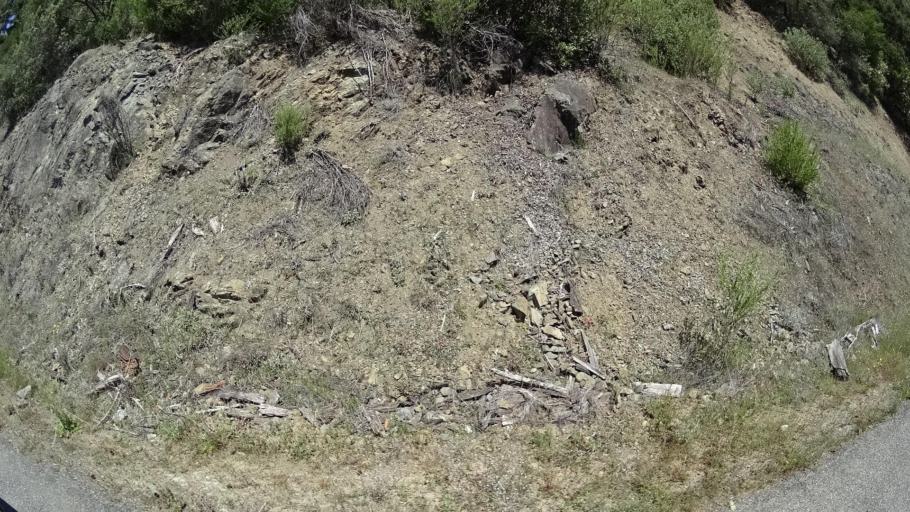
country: US
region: California
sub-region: Humboldt County
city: Redway
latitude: 40.1942
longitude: -123.5513
